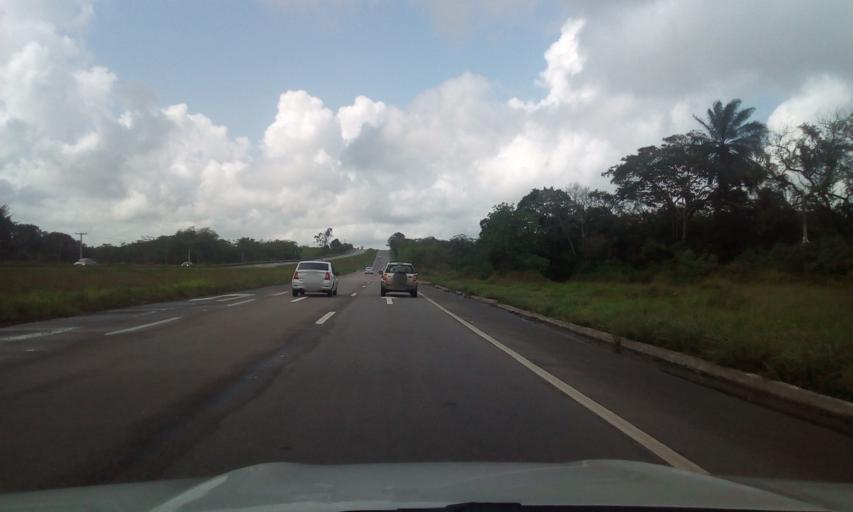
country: BR
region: Paraiba
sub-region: Alhandra
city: Alhandra
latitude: -7.3826
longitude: -34.9574
